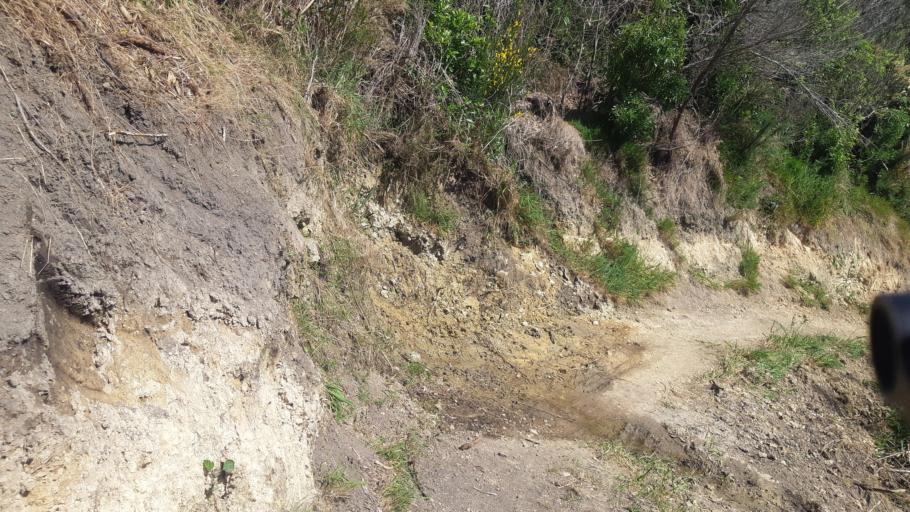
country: NZ
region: Marlborough
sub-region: Marlborough District
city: Picton
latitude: -41.2677
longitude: 174.0272
